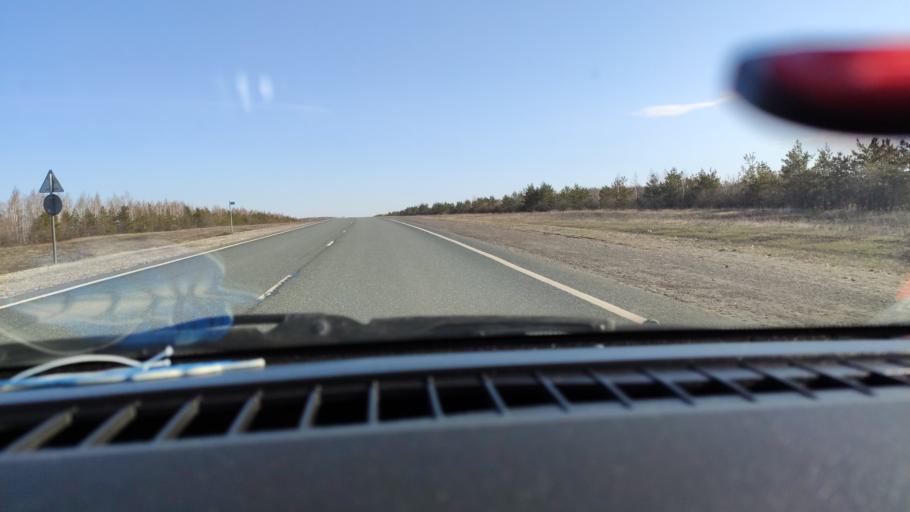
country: RU
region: Samara
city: Syzran'
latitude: 52.8775
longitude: 48.2905
